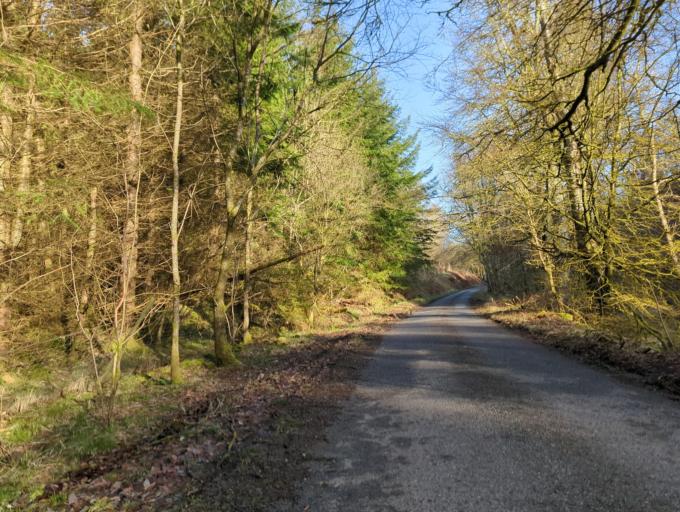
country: GB
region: Scotland
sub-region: Perth and Kinross
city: Methven
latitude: 56.4599
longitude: -3.5898
